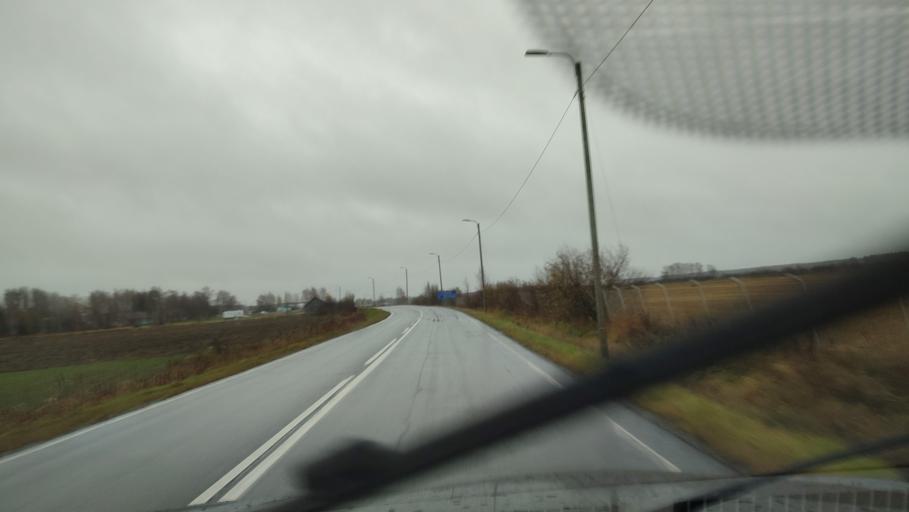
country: FI
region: Ostrobothnia
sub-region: Vaasa
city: Ristinummi
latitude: 63.0448
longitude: 21.7490
